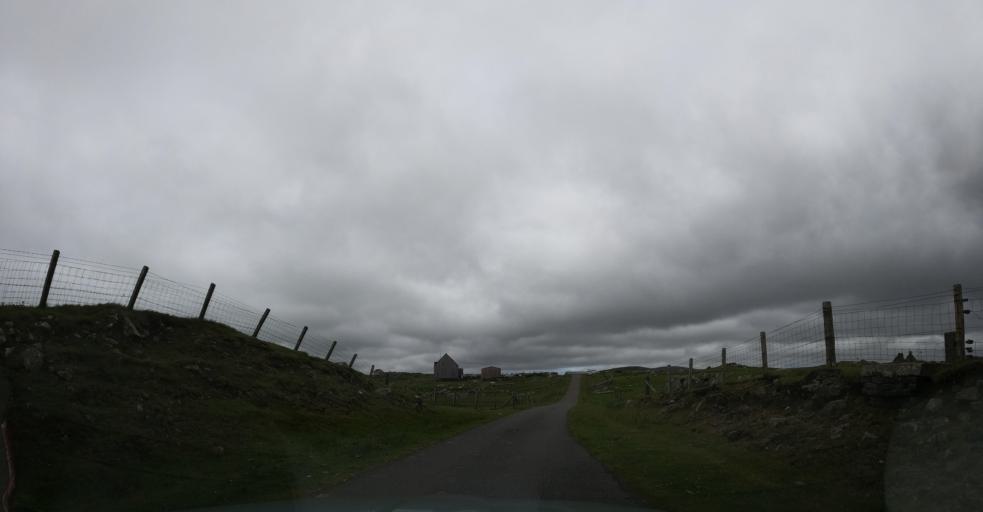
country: GB
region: Scotland
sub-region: Eilean Siar
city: Isle of North Uist
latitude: 57.5456
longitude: -7.3444
